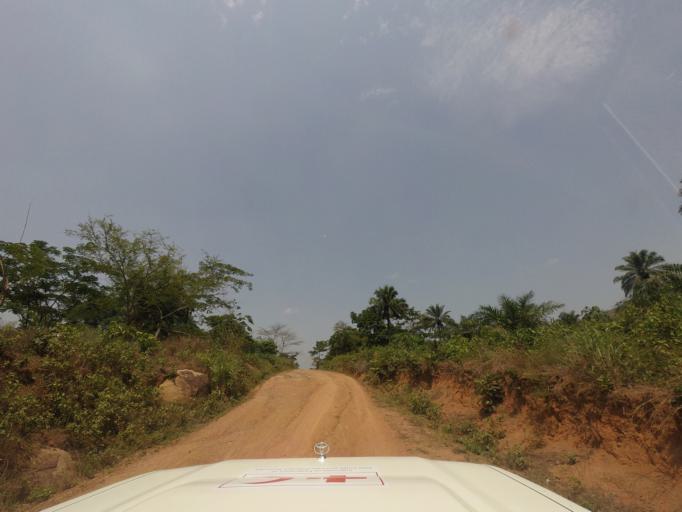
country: LR
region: Lofa
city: Voinjama
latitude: 8.4393
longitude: -9.7326
